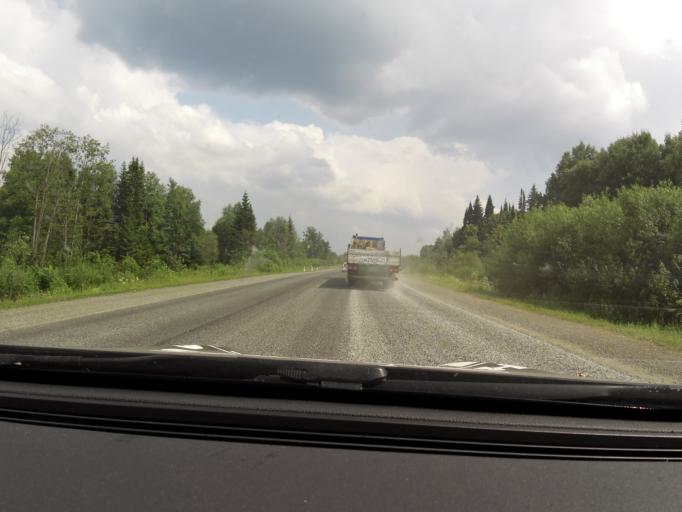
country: RU
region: Sverdlovsk
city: Ufimskiy
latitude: 56.7706
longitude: 58.1203
